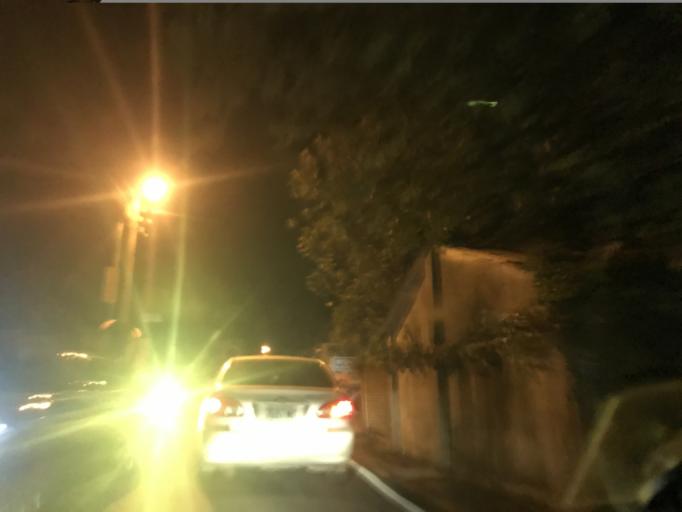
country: TW
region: Taiwan
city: Daxi
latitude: 24.8562
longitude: 121.2127
